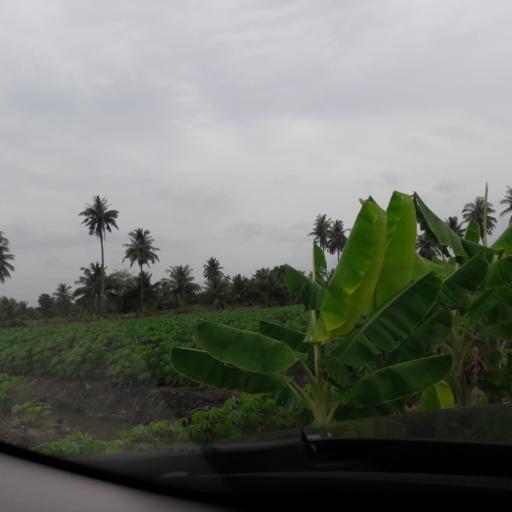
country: TH
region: Ratchaburi
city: Damnoen Saduak
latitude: 13.5780
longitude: 99.9437
